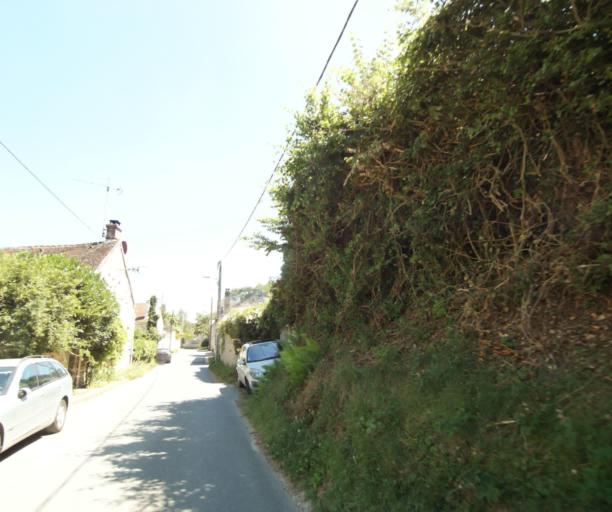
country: FR
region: Ile-de-France
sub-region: Departement de Seine-et-Marne
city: Noisy-sur-Ecole
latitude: 48.3680
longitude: 2.5052
